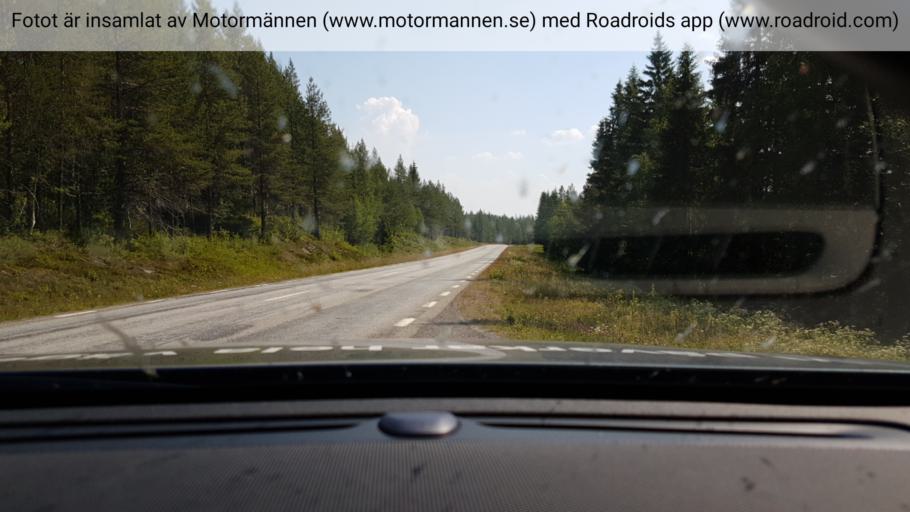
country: SE
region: Vaesterbotten
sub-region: Storumans Kommun
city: Fristad
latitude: 65.3925
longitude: 16.4597
